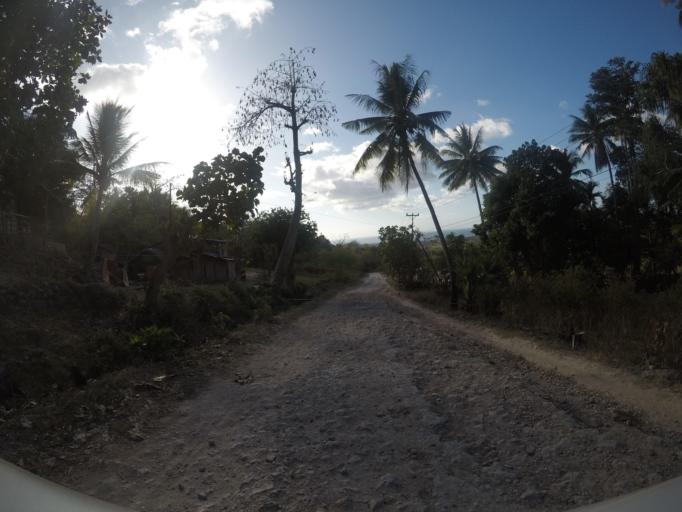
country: TL
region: Lautem
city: Lospalos
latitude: -8.4359
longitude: 126.8502
